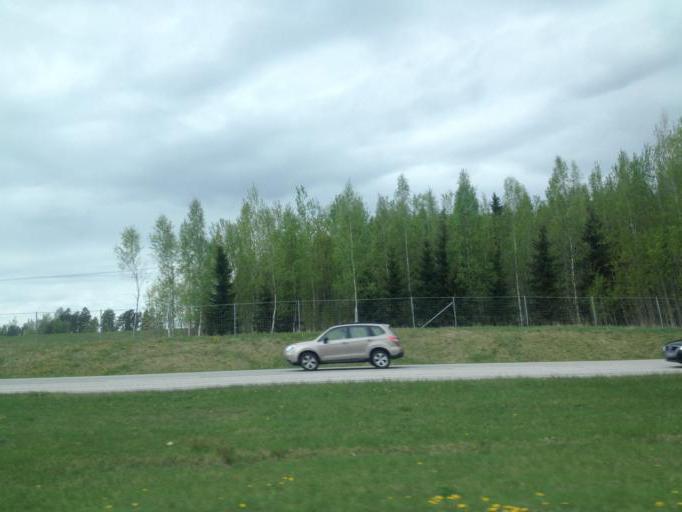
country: FI
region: Uusimaa
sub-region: Helsinki
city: Nurmijaervi
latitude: 60.3975
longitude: 24.8159
